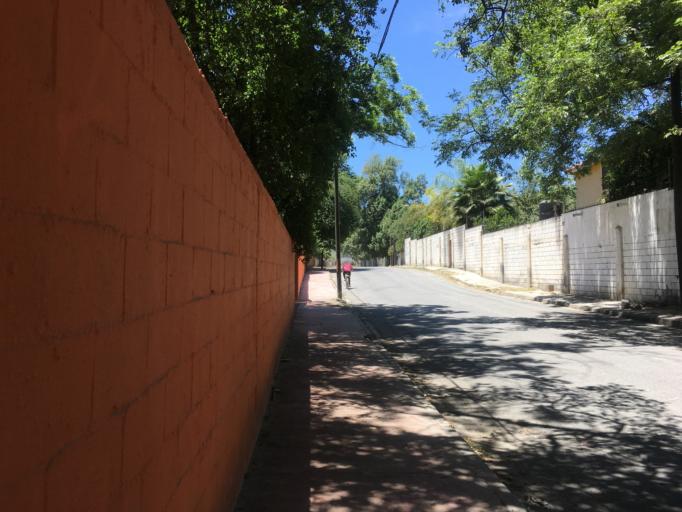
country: MX
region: Nuevo Leon
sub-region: Garcia
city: Las Torres de Guadalupe
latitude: 25.8101
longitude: -100.6109
